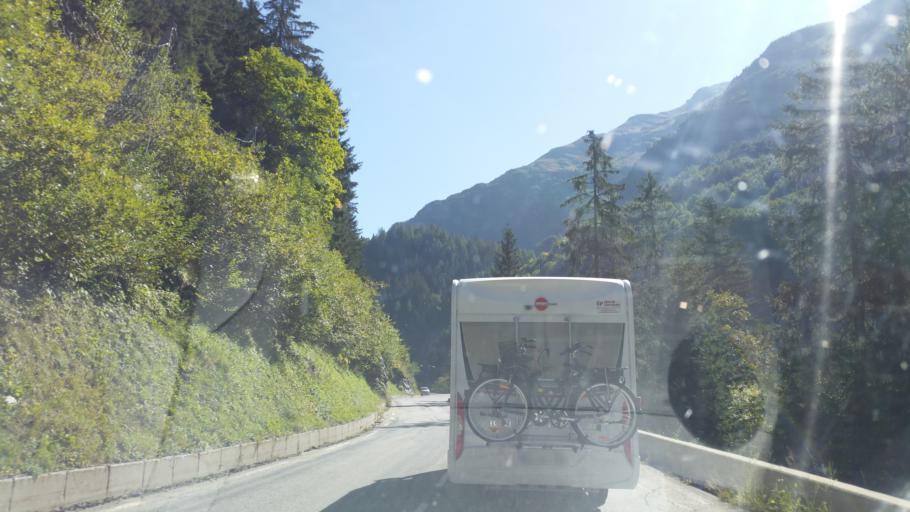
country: FR
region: Rhone-Alpes
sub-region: Departement de la Savoie
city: Tignes
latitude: 45.5543
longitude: 6.9017
